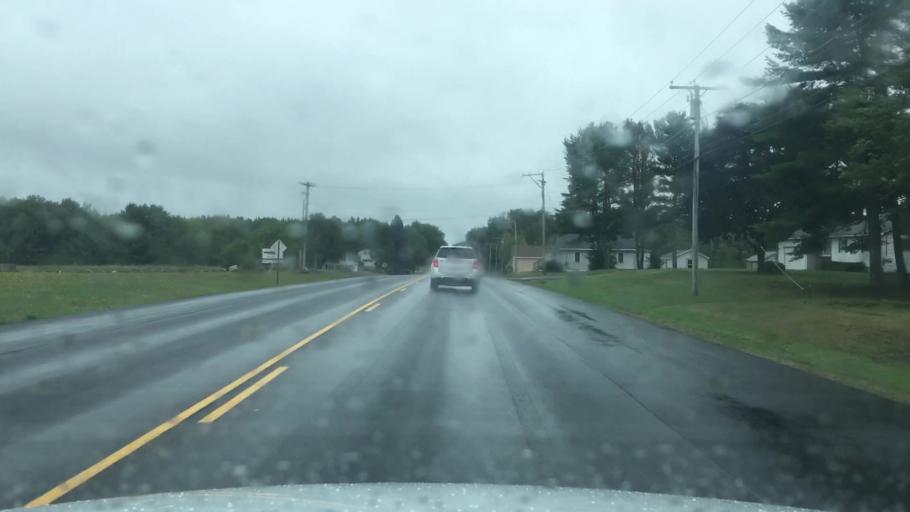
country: US
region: Maine
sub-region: Penobscot County
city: Hampden
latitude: 44.7660
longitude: -68.8537
